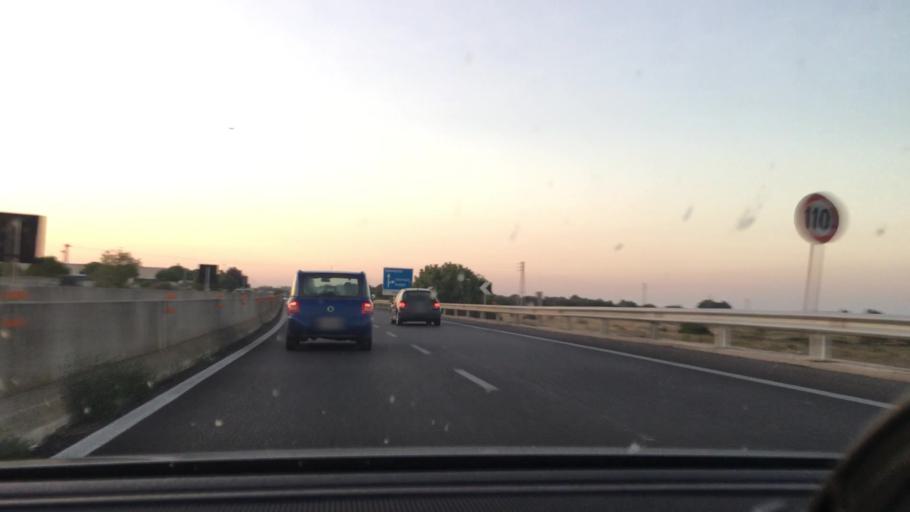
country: IT
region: Apulia
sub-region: Provincia di Lecce
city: Surbo
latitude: 40.3939
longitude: 18.1185
